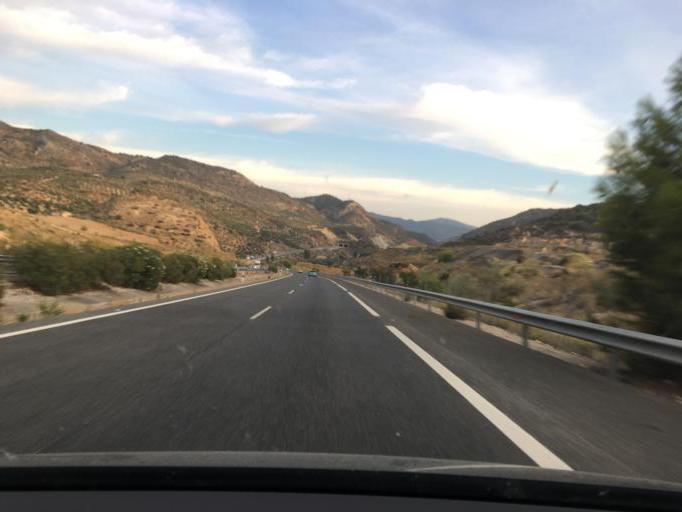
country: ES
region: Andalusia
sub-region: Provincia de Jaen
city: Pegalajar
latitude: 37.7164
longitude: -3.6479
